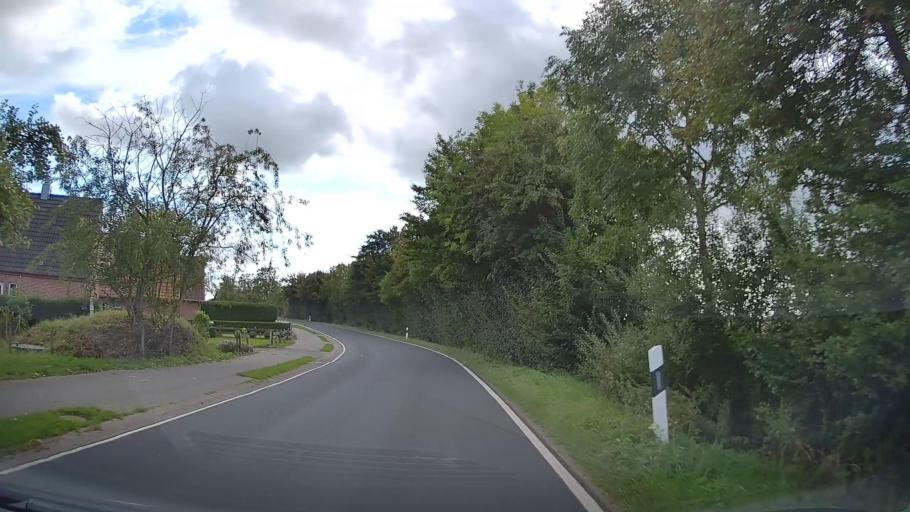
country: DE
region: Schleswig-Holstein
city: Steinberg
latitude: 54.7611
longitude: 9.7997
